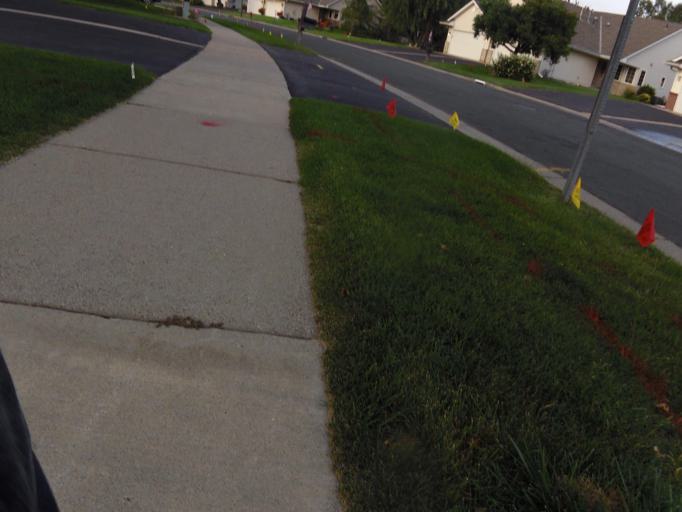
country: US
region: Minnesota
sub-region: Scott County
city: Prior Lake
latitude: 44.7010
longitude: -93.4489
